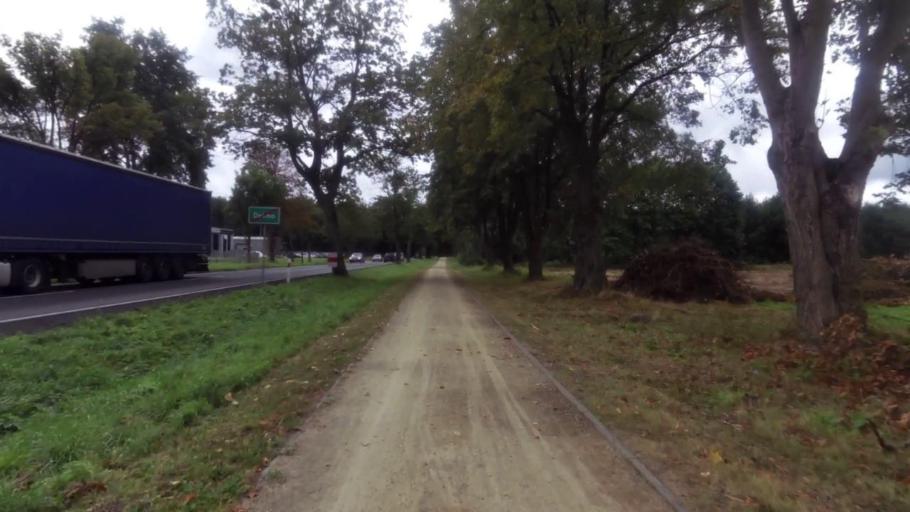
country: PL
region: West Pomeranian Voivodeship
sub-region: Powiat mysliborski
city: Debno
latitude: 52.7238
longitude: 14.6936
